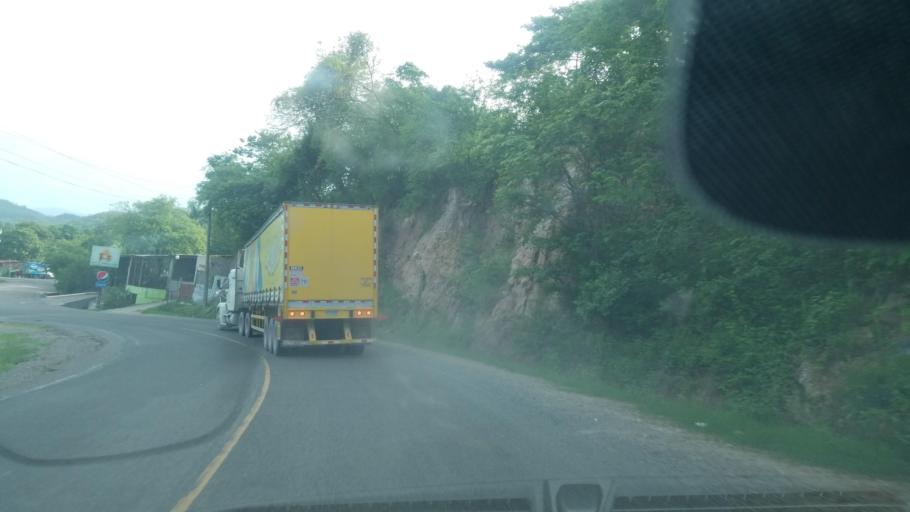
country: HN
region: Santa Barbara
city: Ilama
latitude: 15.0678
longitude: -88.2299
